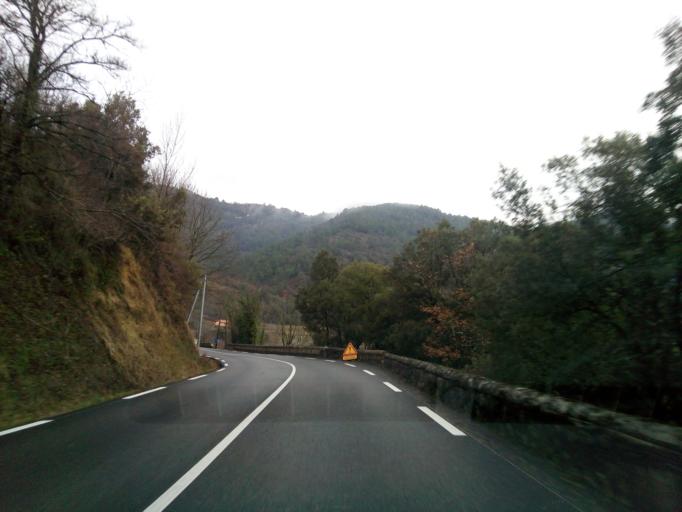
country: FR
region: Rhone-Alpes
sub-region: Departement de l'Ardeche
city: Saint-Sauveur-de-Montagut
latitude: 44.8143
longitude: 4.6399
